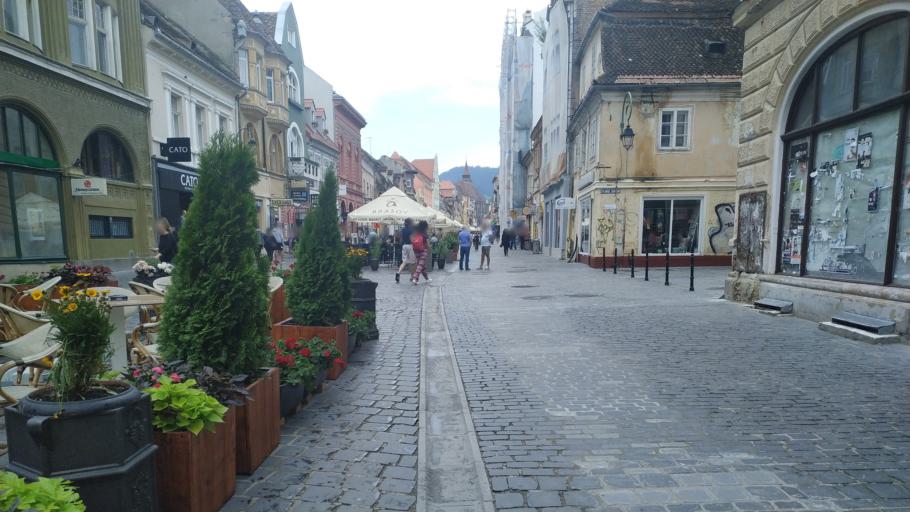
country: RO
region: Brasov
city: Brasov
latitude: 45.6441
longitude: 25.5941
